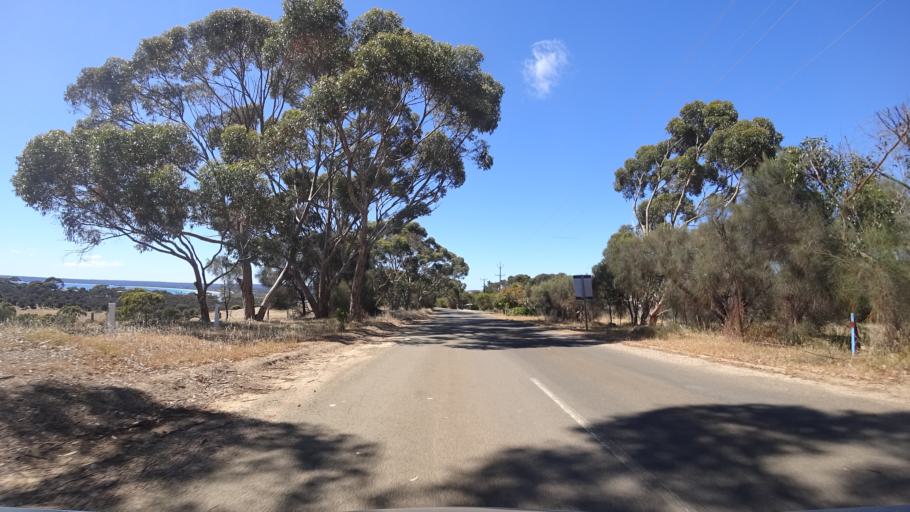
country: AU
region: South Australia
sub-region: Kangaroo Island
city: Kingscote
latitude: -35.7757
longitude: 137.7643
